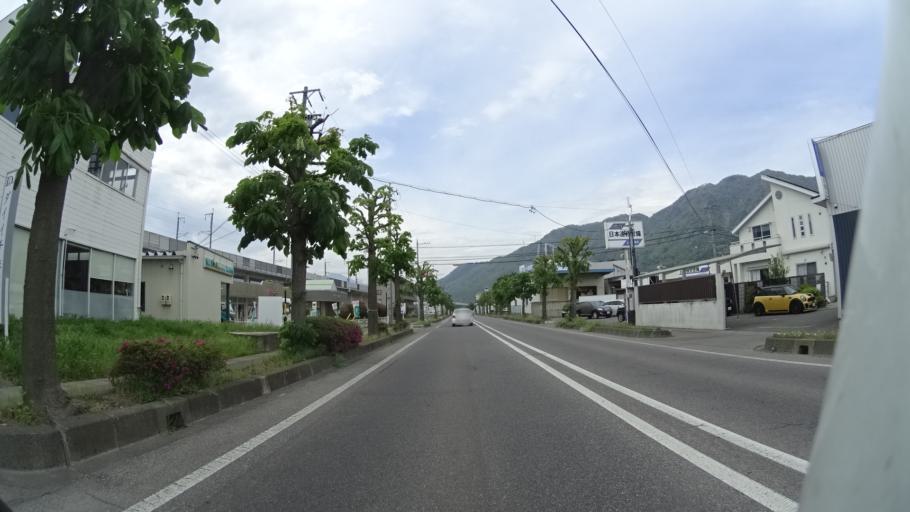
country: JP
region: Nagano
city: Ueda
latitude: 36.4084
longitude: 138.2319
